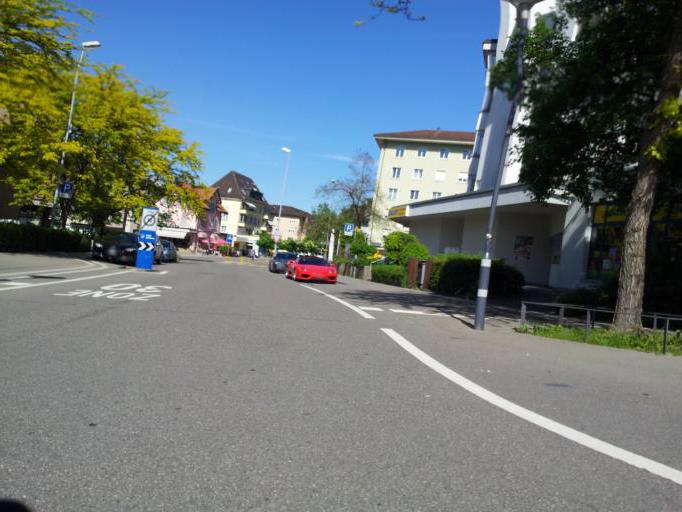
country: CH
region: Zurich
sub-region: Bezirk Dietikon
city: Schlieren
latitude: 47.3958
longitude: 8.4471
